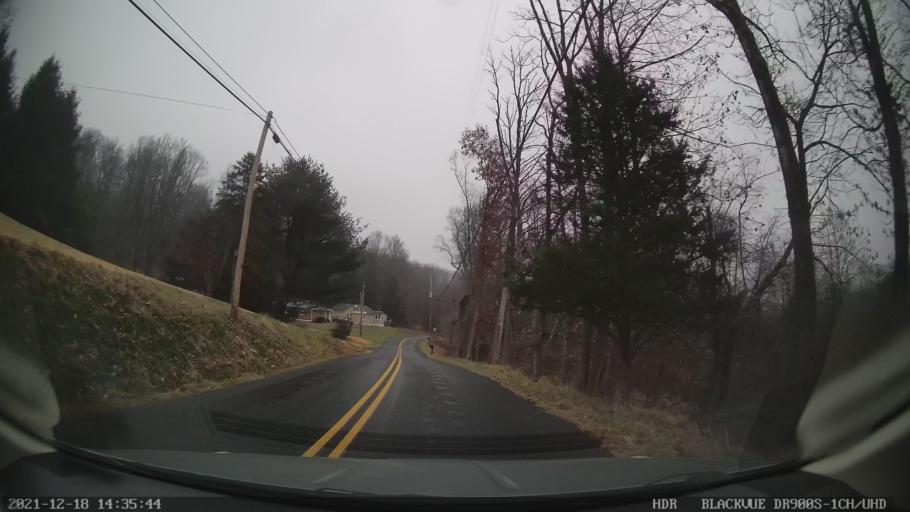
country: US
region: Pennsylvania
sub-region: Berks County
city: New Berlinville
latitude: 40.3848
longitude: -75.6581
